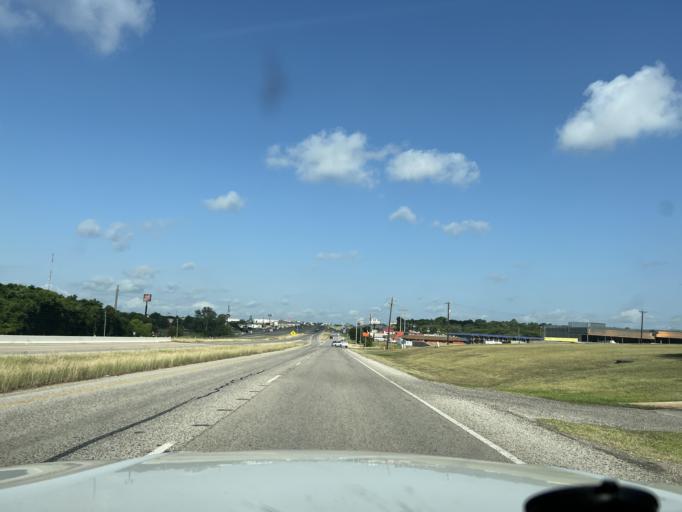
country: US
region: Texas
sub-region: Washington County
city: Brenham
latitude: 30.1429
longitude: -96.3865
